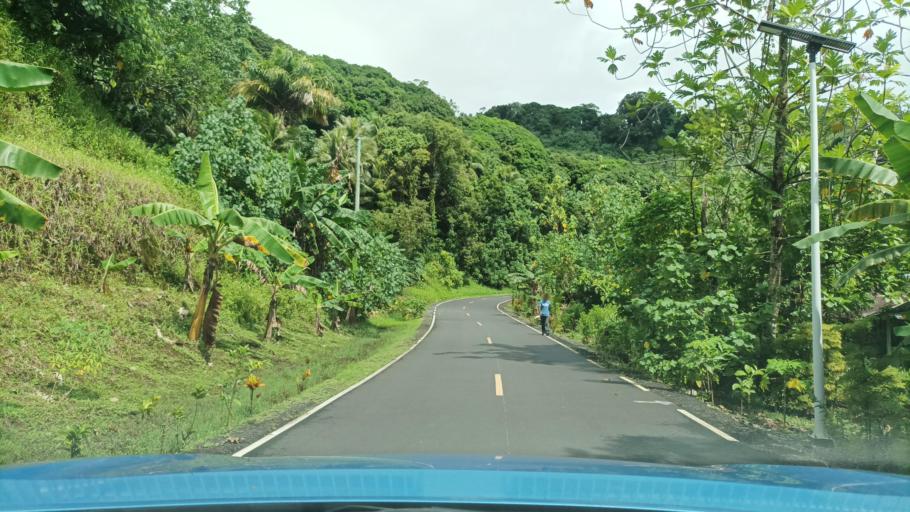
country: FM
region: Pohnpei
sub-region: Madolenihm Municipality
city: Madolenihm Municipality Government
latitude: 6.8696
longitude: 158.3290
